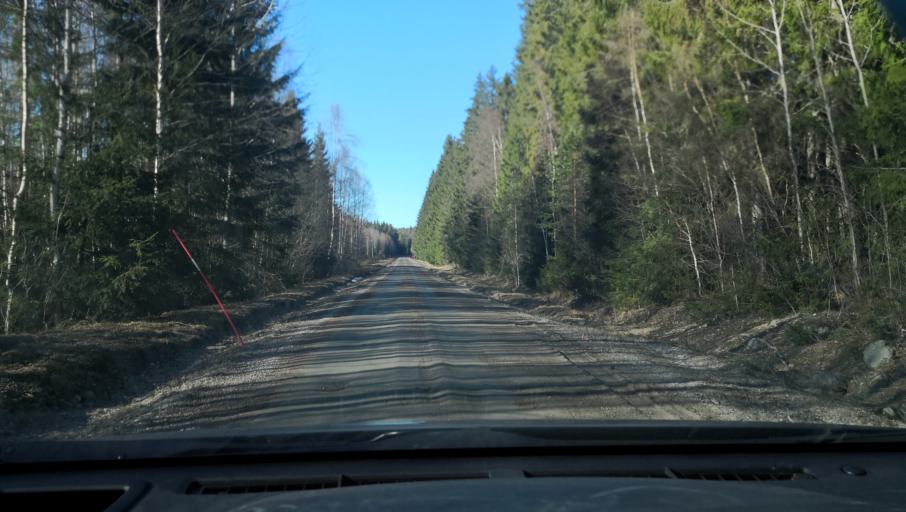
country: SE
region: Vaestmanland
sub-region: Sala Kommun
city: Sala
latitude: 60.1368
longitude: 16.6494
